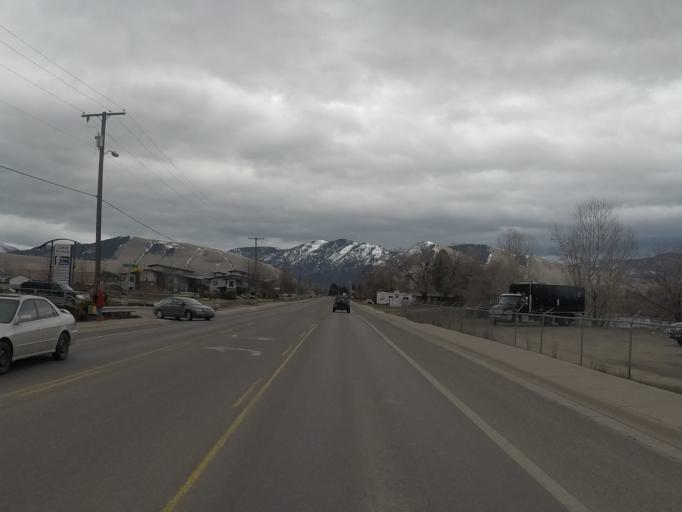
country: US
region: Montana
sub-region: Missoula County
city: Orchard Homes
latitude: 46.8831
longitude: -114.0318
